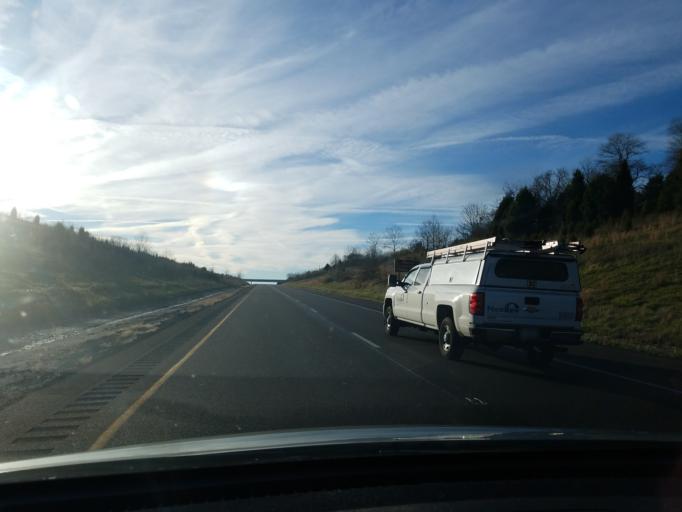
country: US
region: Indiana
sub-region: Crawford County
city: English
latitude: 38.2460
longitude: -86.4233
